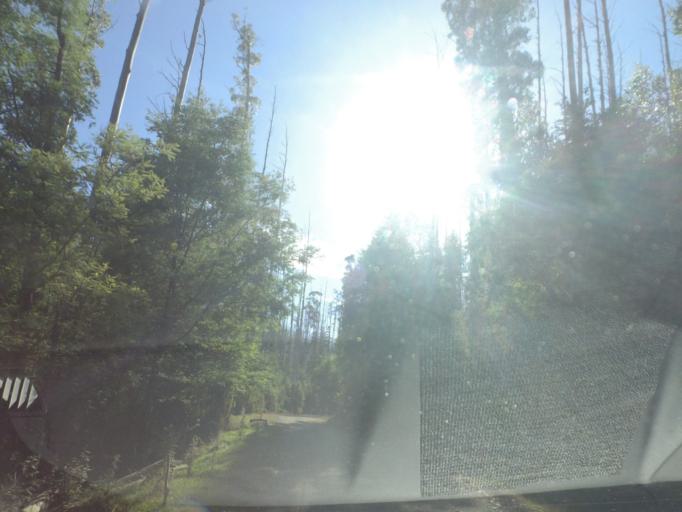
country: AU
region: Victoria
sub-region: Yarra Ranges
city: Millgrove
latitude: -37.5034
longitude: 145.8107
